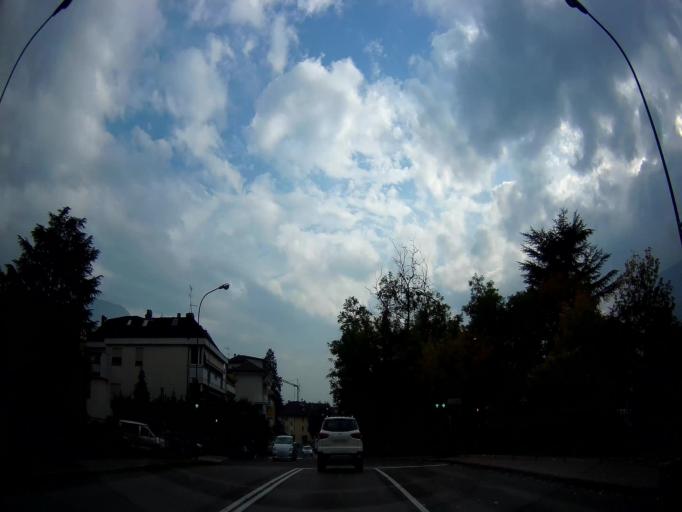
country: IT
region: Trentino-Alto Adige
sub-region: Bolzano
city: Merano
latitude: 46.6688
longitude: 11.1531
